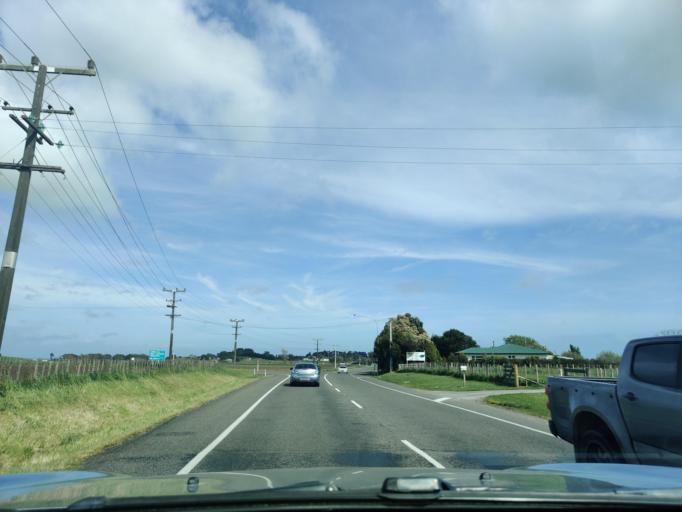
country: NZ
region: Manawatu-Wanganui
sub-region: Wanganui District
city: Wanganui
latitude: -39.8886
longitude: 175.0064
